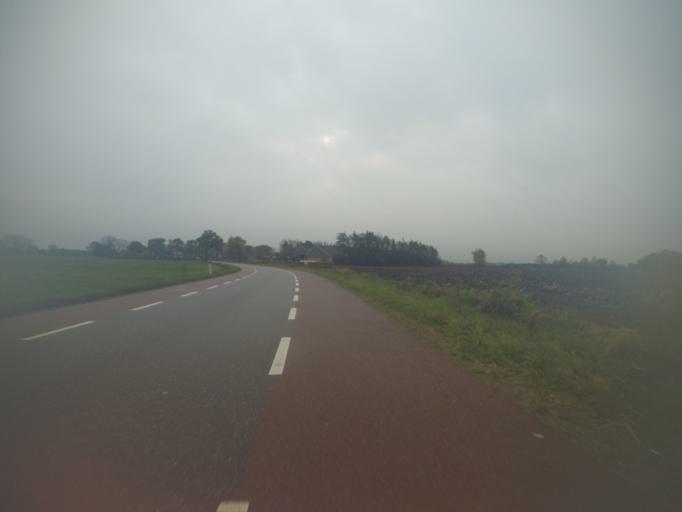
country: NL
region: Gelderland
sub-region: Gemeente Barneveld
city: Barneveld
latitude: 52.1081
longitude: 5.5587
